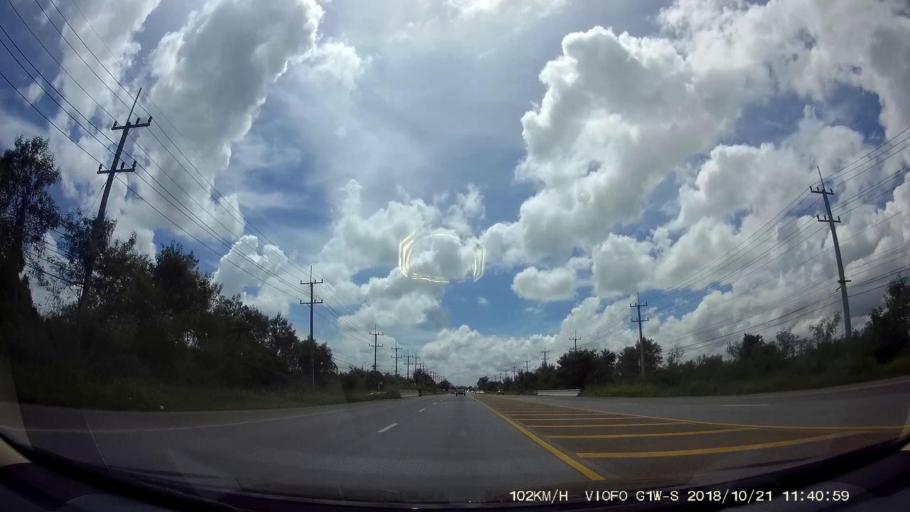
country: TH
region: Chaiyaphum
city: Chaiyaphum
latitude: 15.7058
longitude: 102.0151
